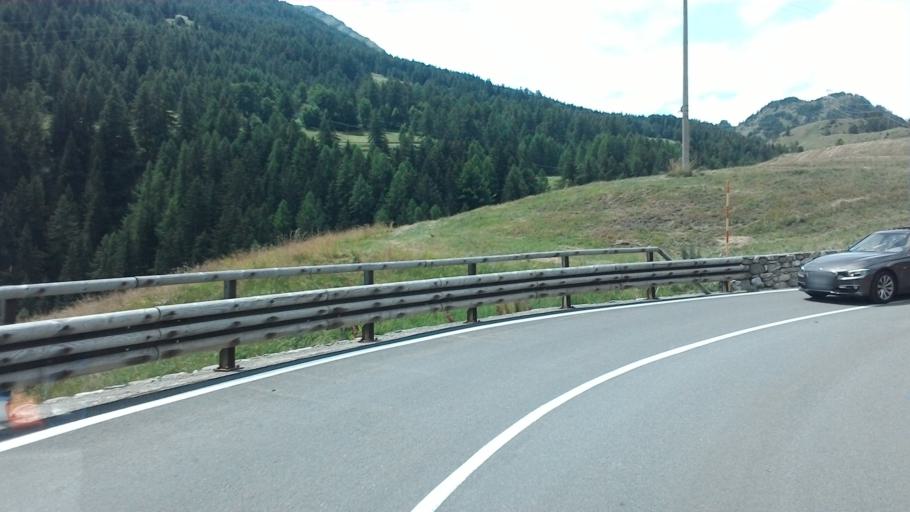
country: IT
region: Aosta Valley
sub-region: Valle d'Aosta
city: La Thuile
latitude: 45.7120
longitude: 6.9366
